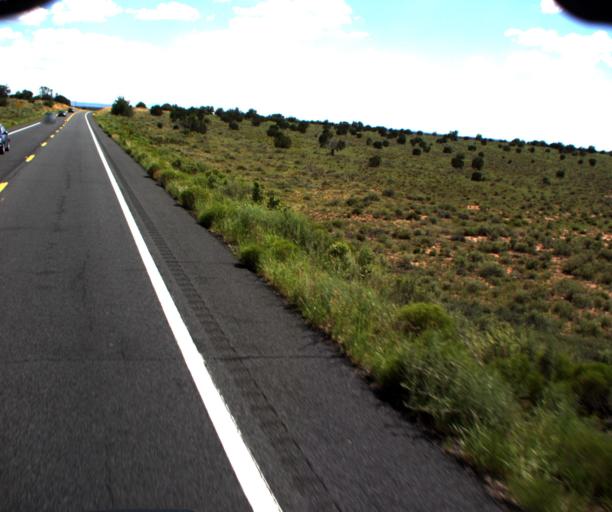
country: US
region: Arizona
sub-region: Coconino County
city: Grand Canyon Village
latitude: 35.7156
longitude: -112.1312
